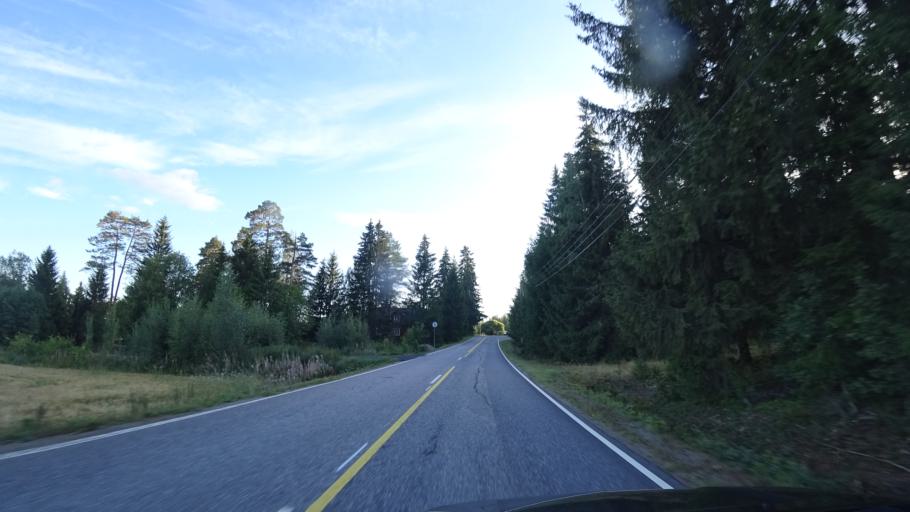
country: FI
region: Haeme
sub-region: Haemeenlinna
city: Lammi
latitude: 61.0081
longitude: 24.8822
